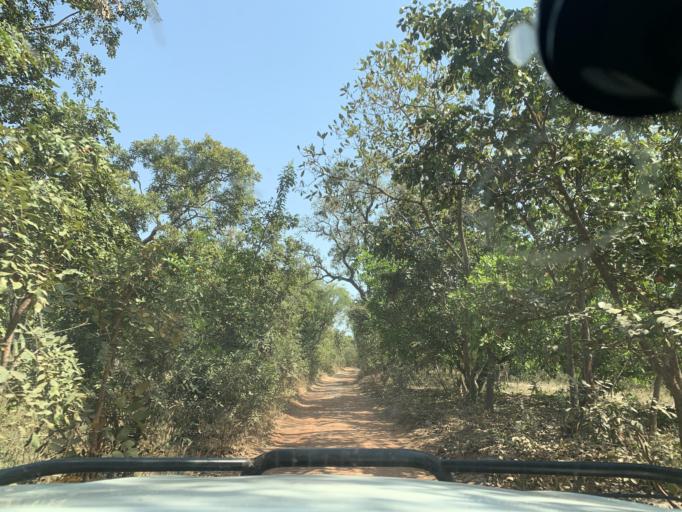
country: ML
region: Sikasso
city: Kolondieba
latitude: 10.8936
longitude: -6.7480
